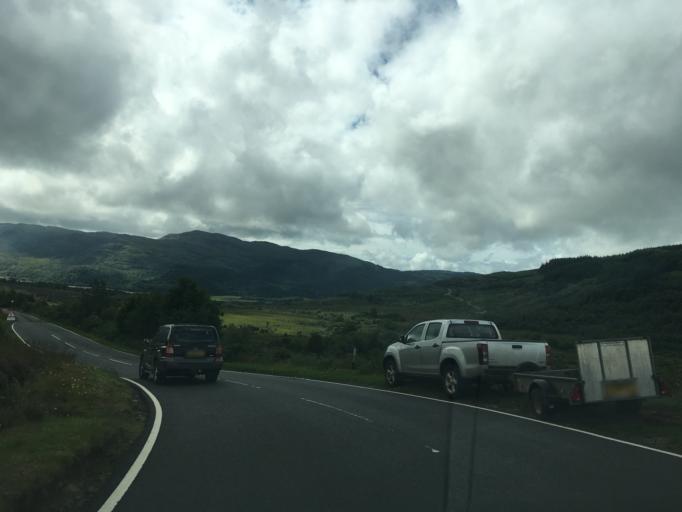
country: GB
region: Scotland
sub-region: Argyll and Bute
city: Port Bannatyne
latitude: 55.9914
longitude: -5.1487
